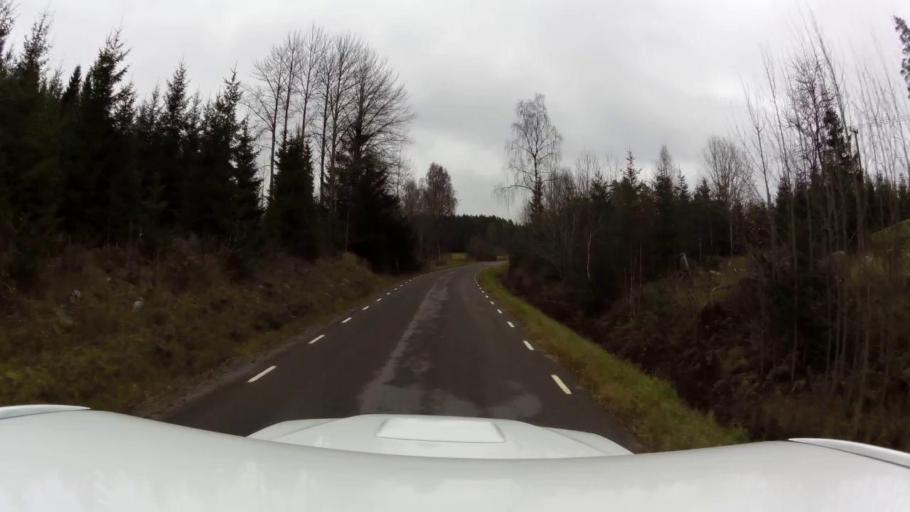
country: SE
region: OEstergoetland
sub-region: Kinda Kommun
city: Rimforsa
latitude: 58.1469
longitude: 15.4761
